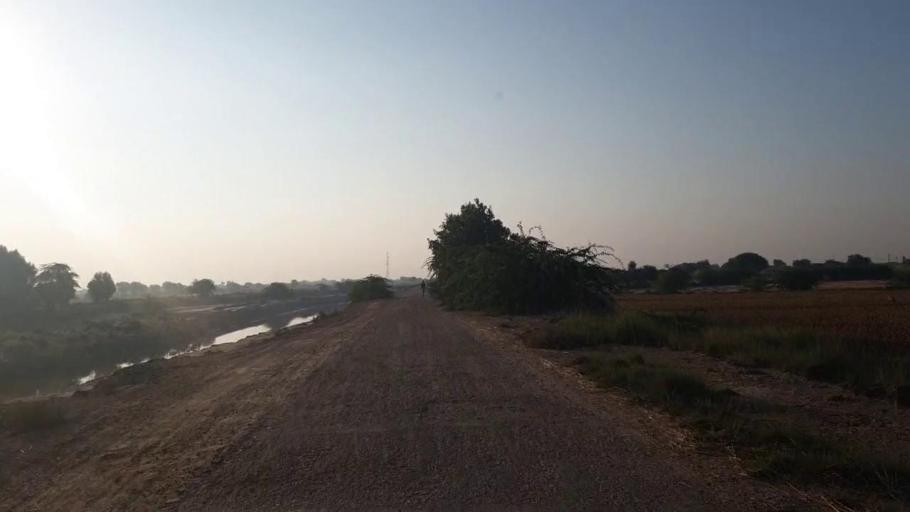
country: PK
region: Sindh
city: Badin
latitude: 24.6562
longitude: 68.7886
